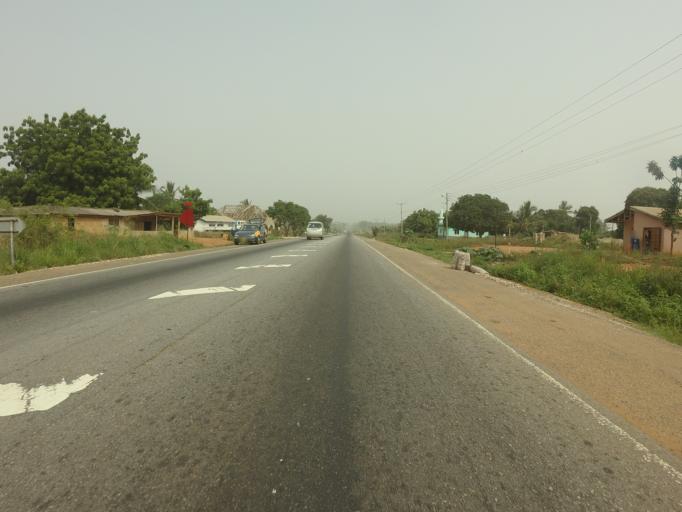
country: GH
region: Volta
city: Anloga
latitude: 5.8906
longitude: 0.4778
